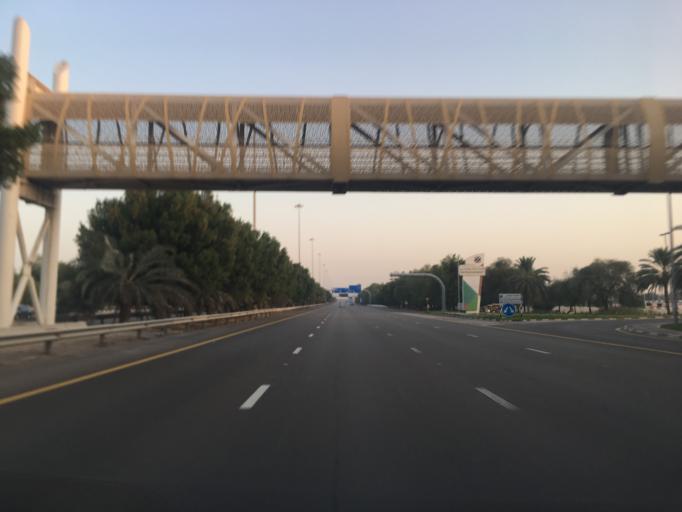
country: AE
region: Abu Dhabi
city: Abu Dhabi
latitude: 24.3641
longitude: 54.5623
